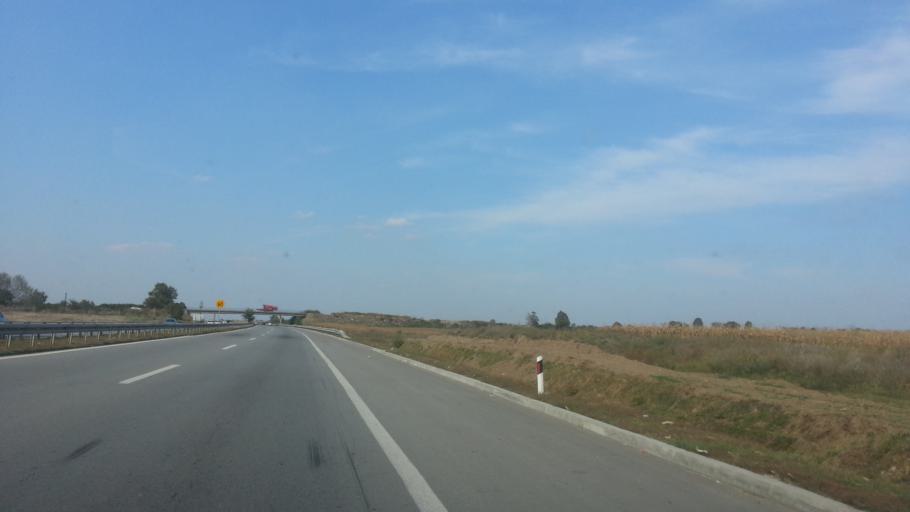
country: RS
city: Novi Banovci
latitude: 44.9129
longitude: 20.3055
